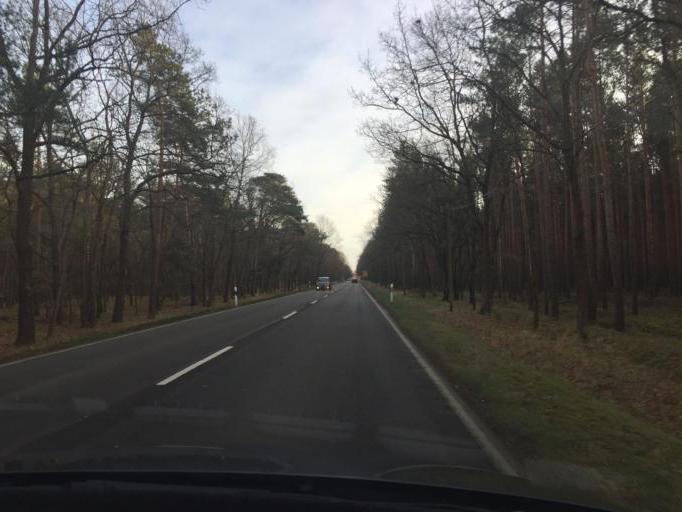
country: DE
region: Brandenburg
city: Cottbus
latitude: 51.7419
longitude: 14.3948
